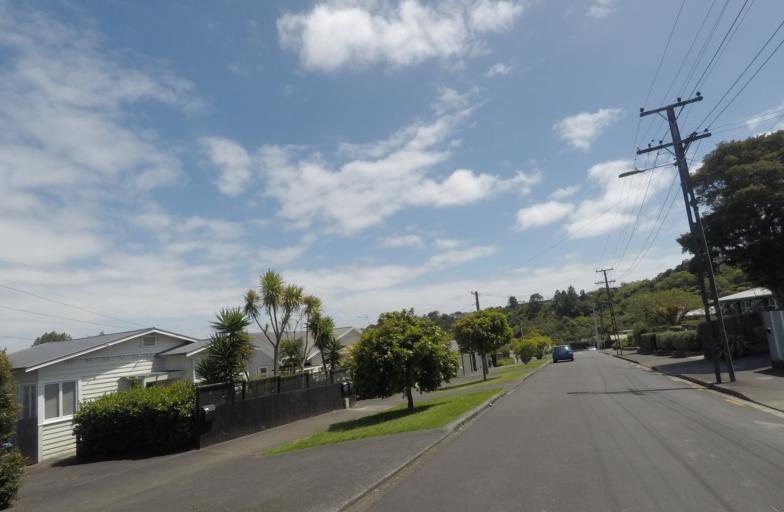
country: NZ
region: Auckland
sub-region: Auckland
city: Auckland
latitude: -36.8705
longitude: 174.7377
